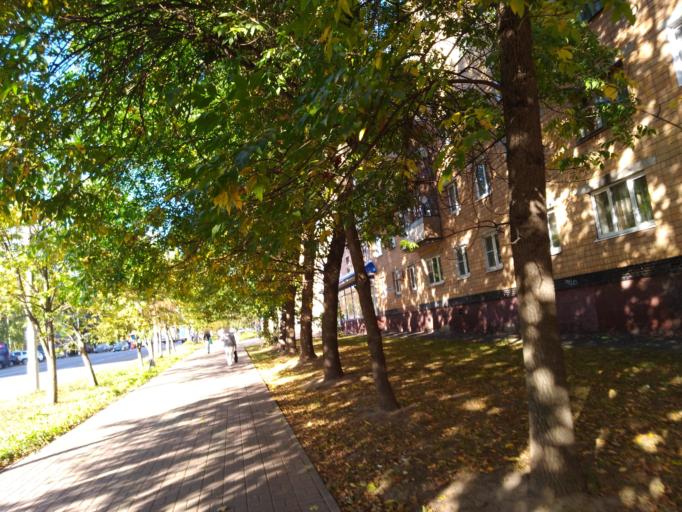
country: RU
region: Kaluga
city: Kaluga
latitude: 54.5266
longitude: 36.2729
